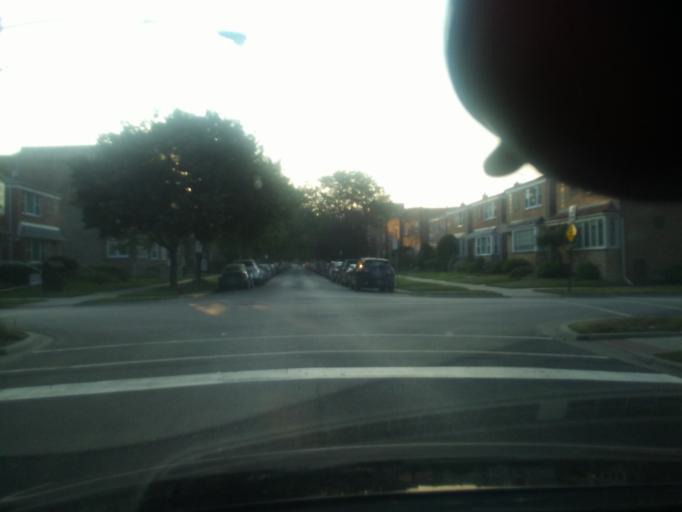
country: US
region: Illinois
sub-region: Cook County
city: Lincolnwood
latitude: 41.9767
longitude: -87.6968
